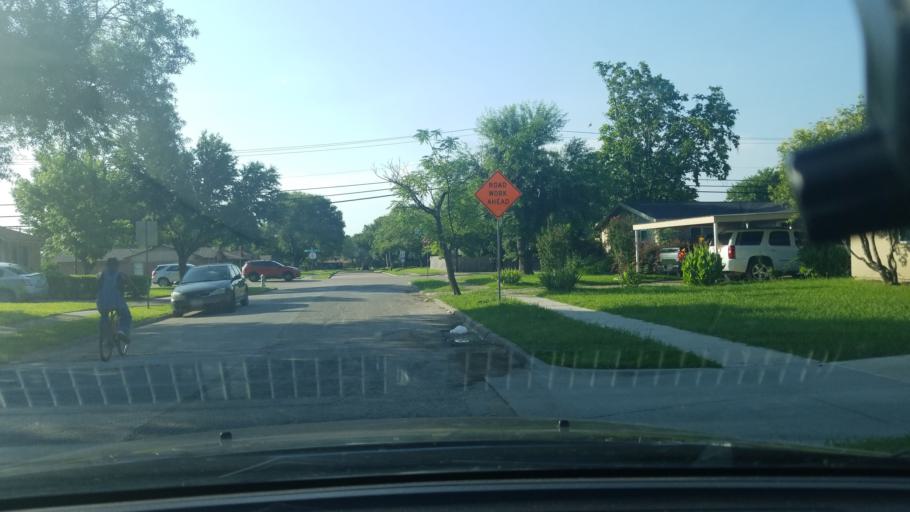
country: US
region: Texas
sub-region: Dallas County
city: Mesquite
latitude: 32.8101
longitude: -96.6371
